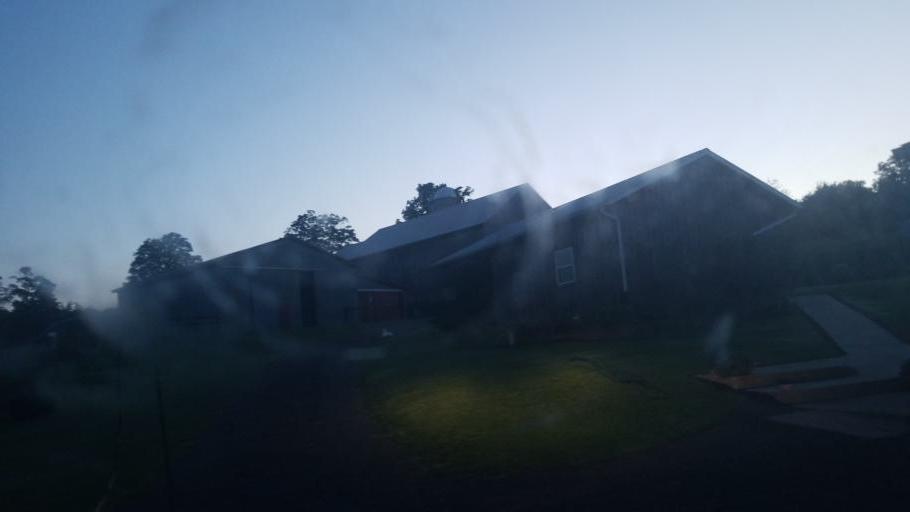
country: US
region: New York
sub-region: Allegany County
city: Andover
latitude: 41.9290
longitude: -77.7861
